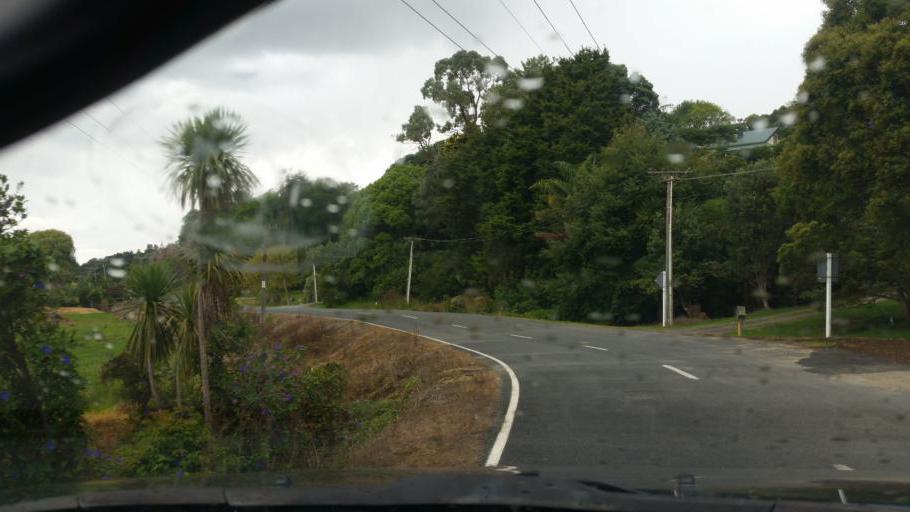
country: NZ
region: Northland
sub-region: Kaipara District
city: Dargaville
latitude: -35.9546
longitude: 173.8596
